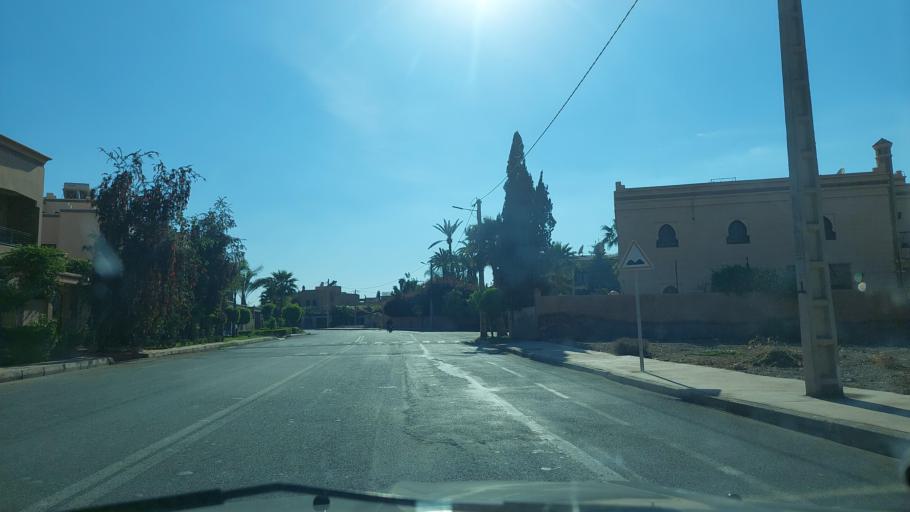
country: MA
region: Marrakech-Tensift-Al Haouz
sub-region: Marrakech
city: Marrakesh
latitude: 31.6655
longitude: -8.0592
